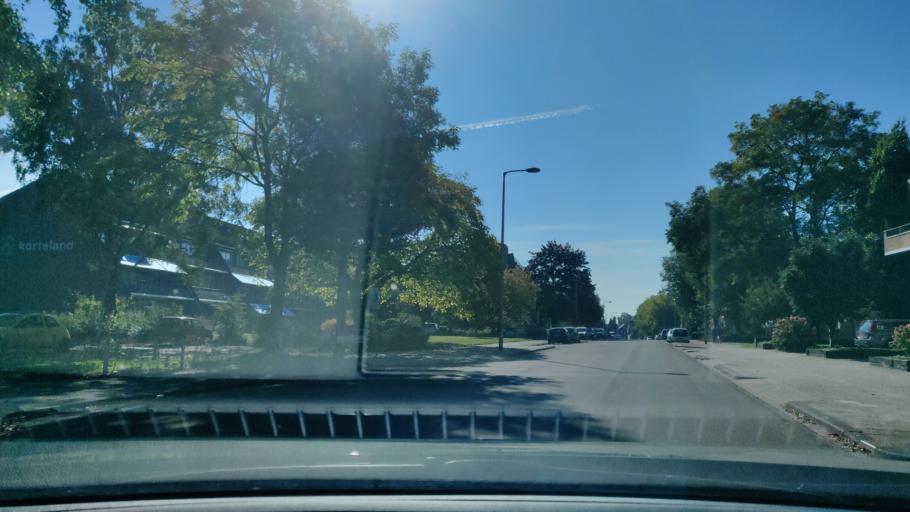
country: NL
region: Overijssel
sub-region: Gemeente Enschede
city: Enschede
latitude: 52.2193
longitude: 6.9051
